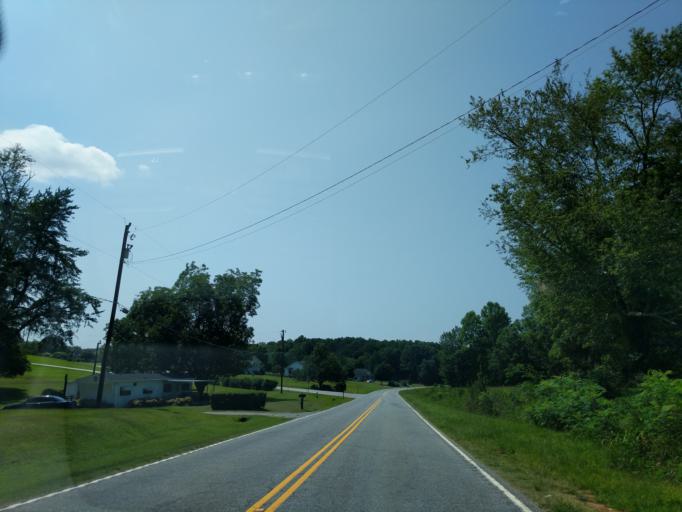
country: US
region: South Carolina
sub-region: Greenville County
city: Greer
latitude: 34.9645
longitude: -82.1907
